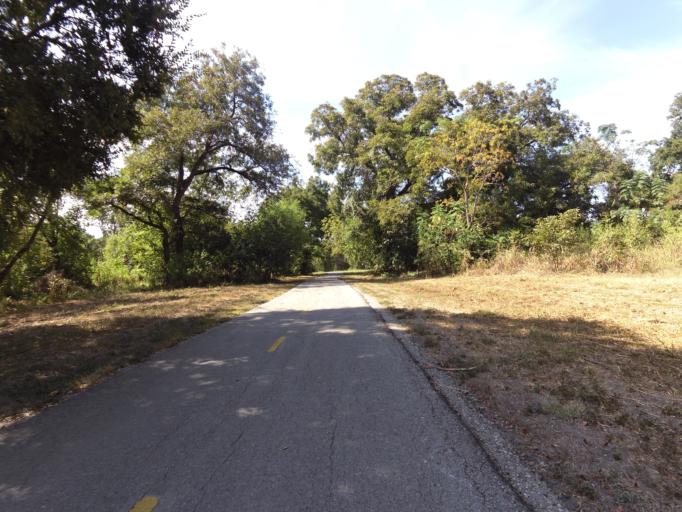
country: US
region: Texas
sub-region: Bexar County
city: Kirby
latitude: 29.4310
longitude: -98.4230
